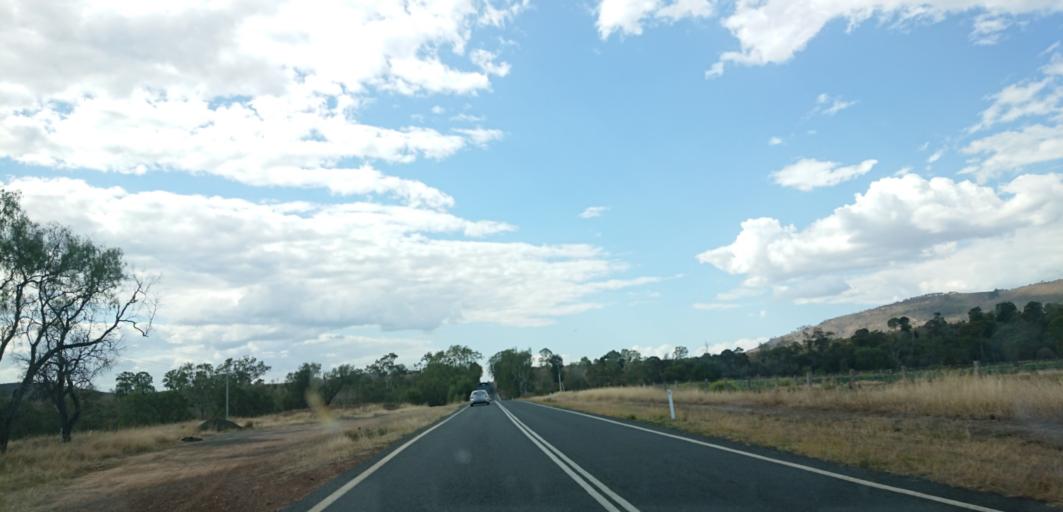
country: AU
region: Queensland
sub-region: Lockyer Valley
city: Gatton
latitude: -27.6621
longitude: 152.1622
